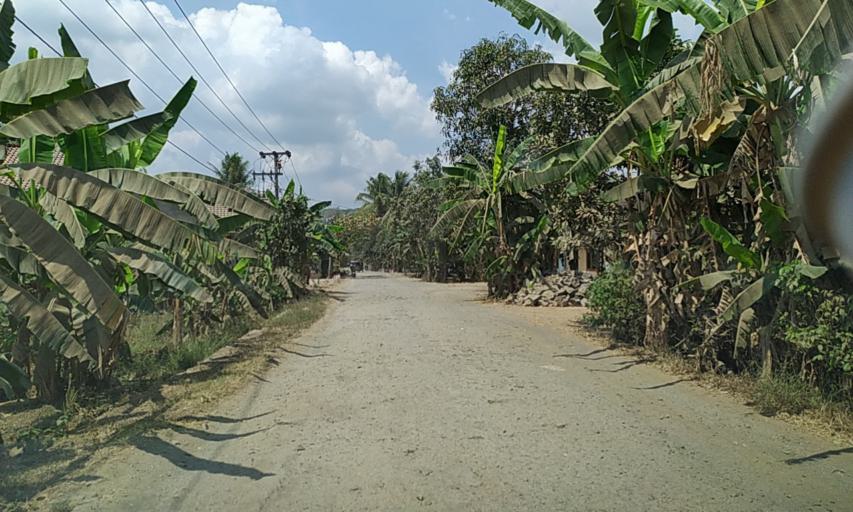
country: ID
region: Central Java
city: Tawangsari
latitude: -7.3866
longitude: 108.7991
